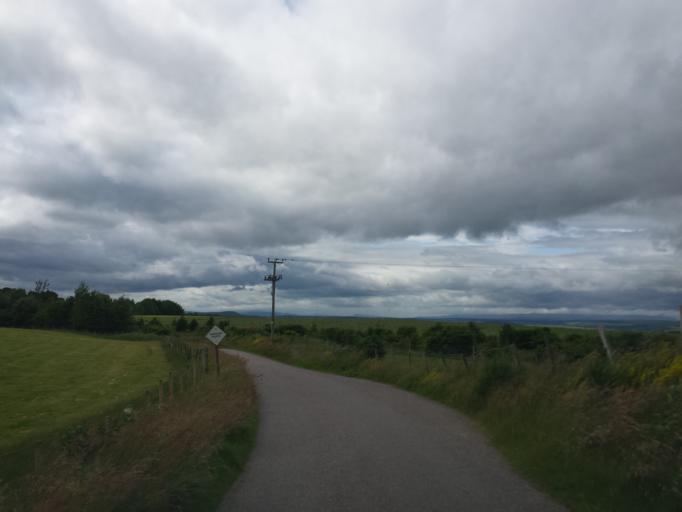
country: GB
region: Scotland
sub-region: Highland
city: Fortrose
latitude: 57.5116
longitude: -4.0306
